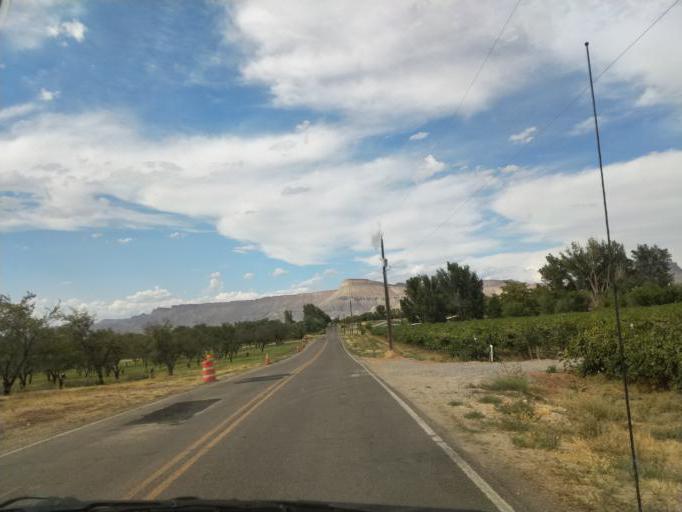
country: US
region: Colorado
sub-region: Mesa County
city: Clifton
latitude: 39.0579
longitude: -108.4133
